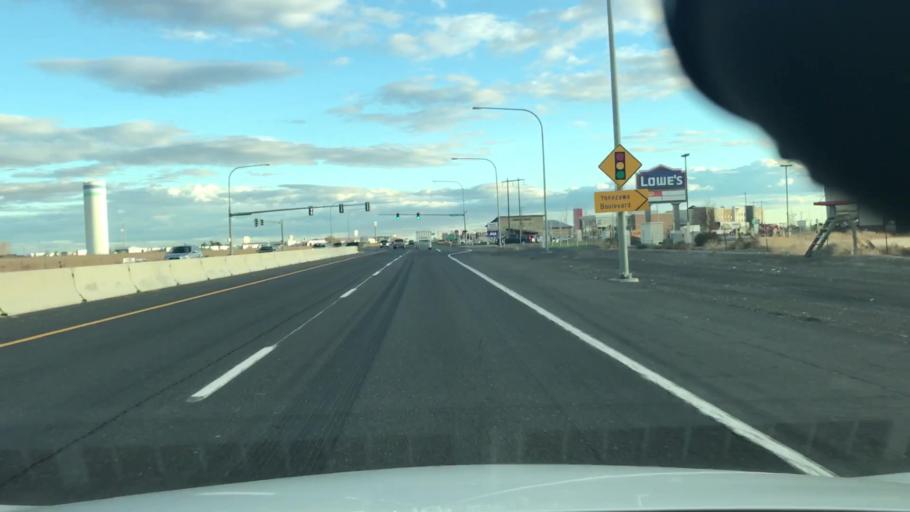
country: US
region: Washington
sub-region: Grant County
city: Moses Lake
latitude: 47.1071
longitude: -119.2532
